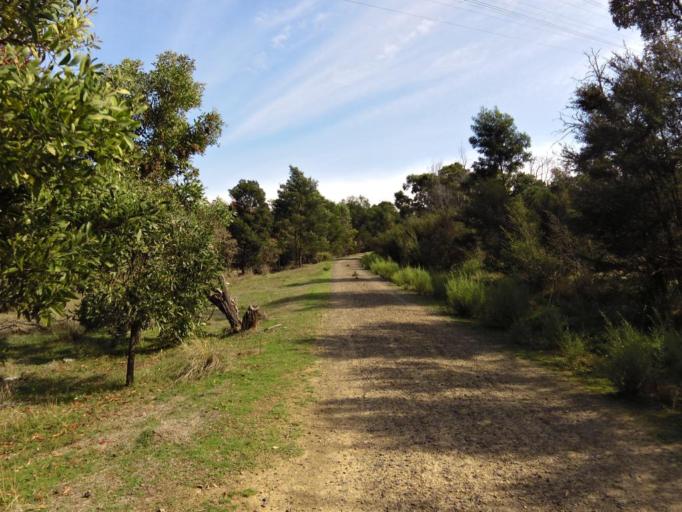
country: AU
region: Victoria
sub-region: Casey
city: Endeavour Hills
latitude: -37.9555
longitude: 145.2611
